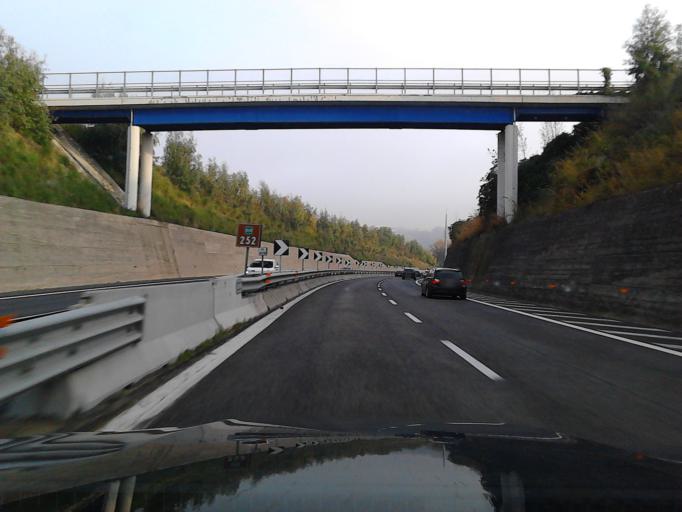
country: IT
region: Abruzzo
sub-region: Provincia di Chieti
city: San Vito Chietino
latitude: 42.2990
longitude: 14.4294
